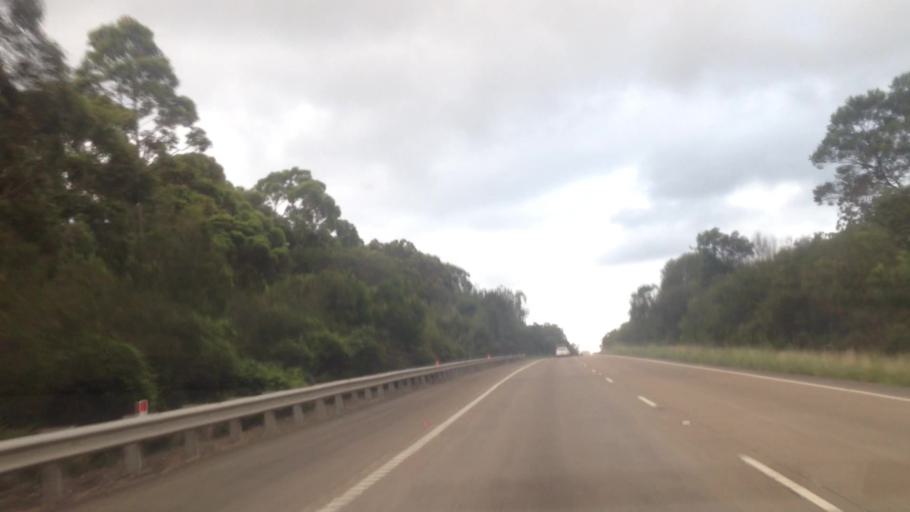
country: AU
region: New South Wales
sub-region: Lake Macquarie Shire
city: Dora Creek
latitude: -33.1540
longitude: 151.4713
